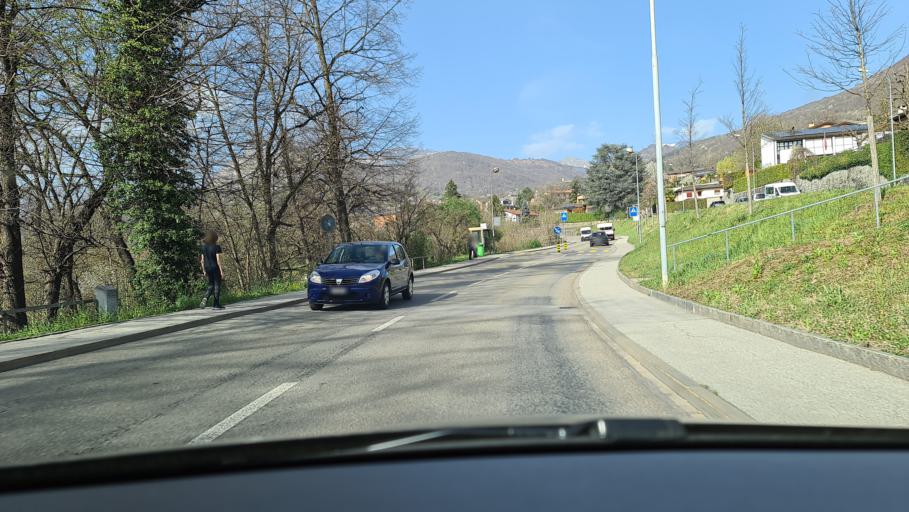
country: CH
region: Ticino
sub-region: Lugano District
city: Cadro
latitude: 46.0406
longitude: 8.9821
